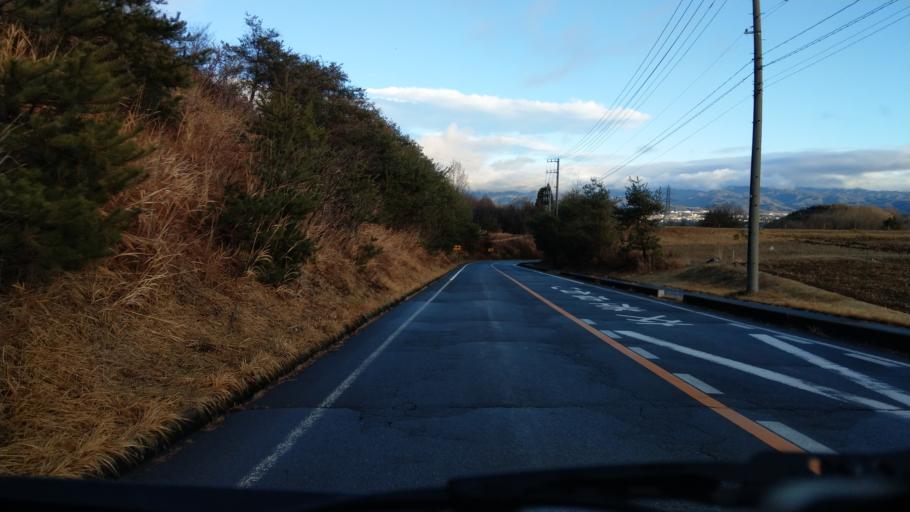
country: JP
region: Nagano
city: Komoro
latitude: 36.3023
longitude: 138.4088
